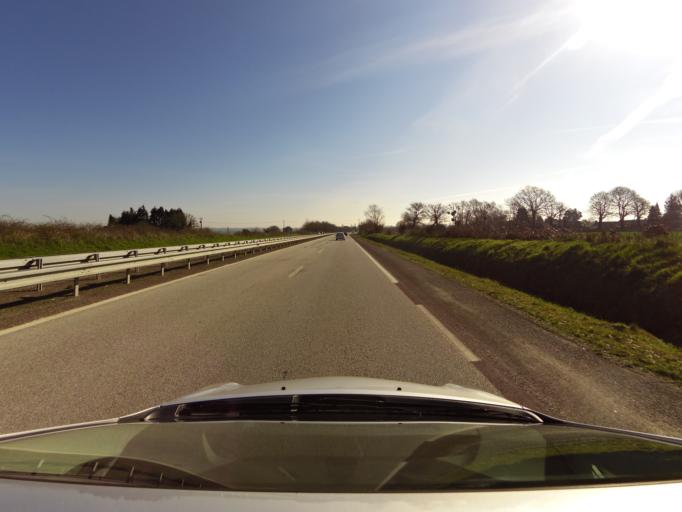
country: FR
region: Brittany
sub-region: Departement du Morbihan
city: Guegon
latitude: 47.9445
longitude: -2.5968
